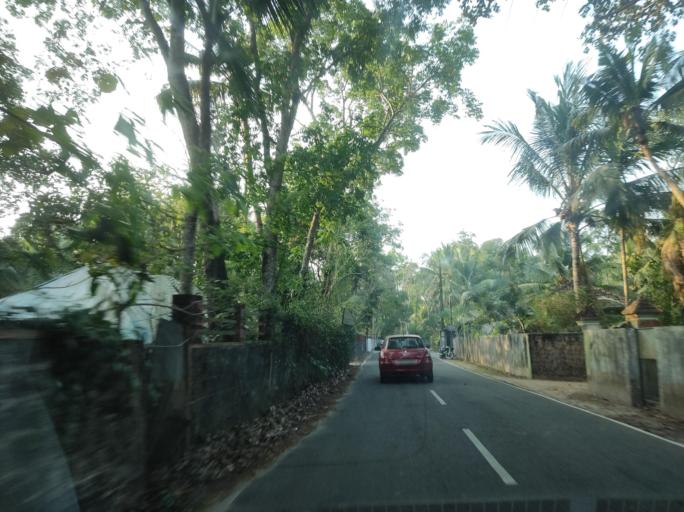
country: IN
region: Kerala
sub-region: Alappuzha
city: Shertallai
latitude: 9.6139
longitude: 76.3131
